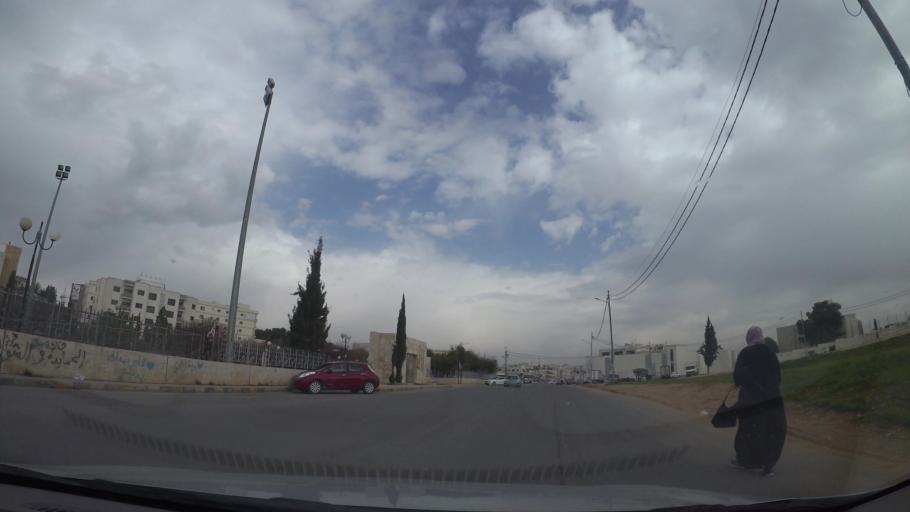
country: JO
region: Amman
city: Umm as Summaq
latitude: 31.8893
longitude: 35.8444
